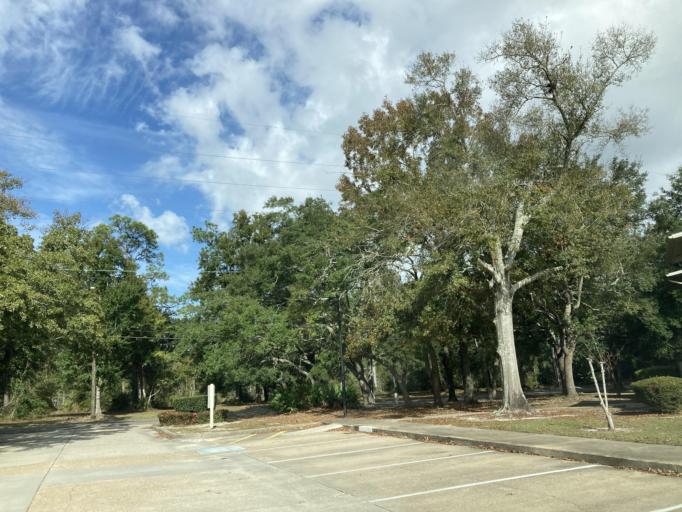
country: US
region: Mississippi
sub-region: Harrison County
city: D'Iberville
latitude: 30.4094
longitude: -88.9732
